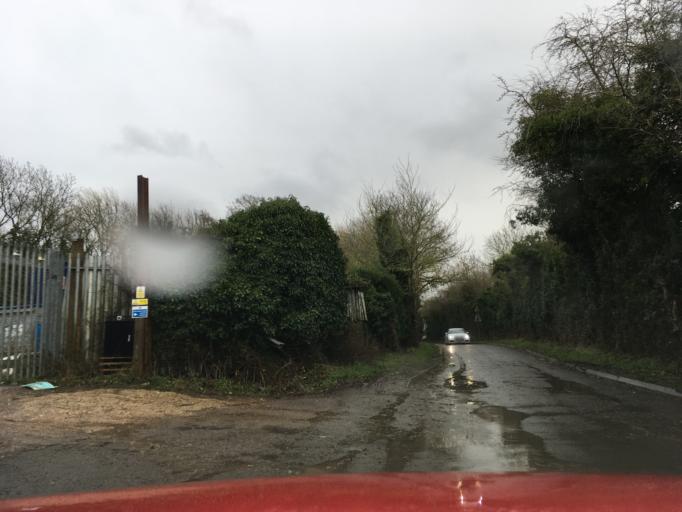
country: GB
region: England
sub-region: Oxfordshire
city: Oxford
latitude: 51.7550
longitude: -1.2811
